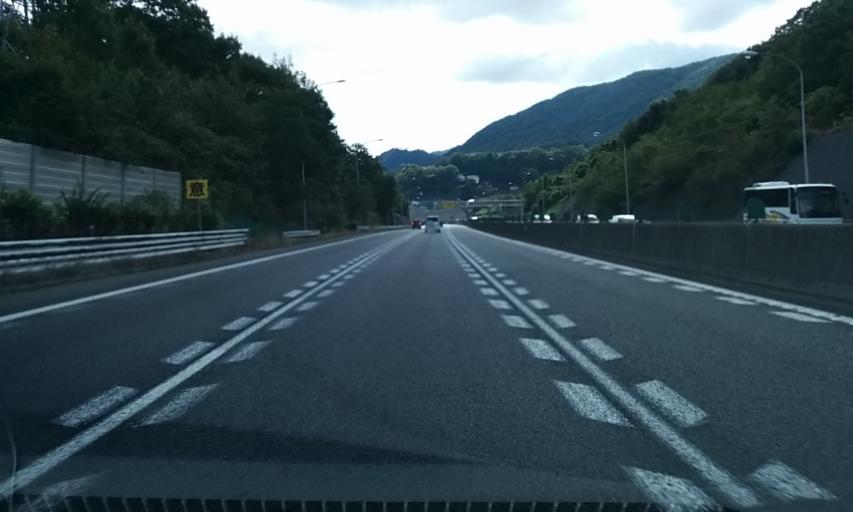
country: JP
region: Hyogo
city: Sandacho
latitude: 34.8329
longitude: 135.2828
